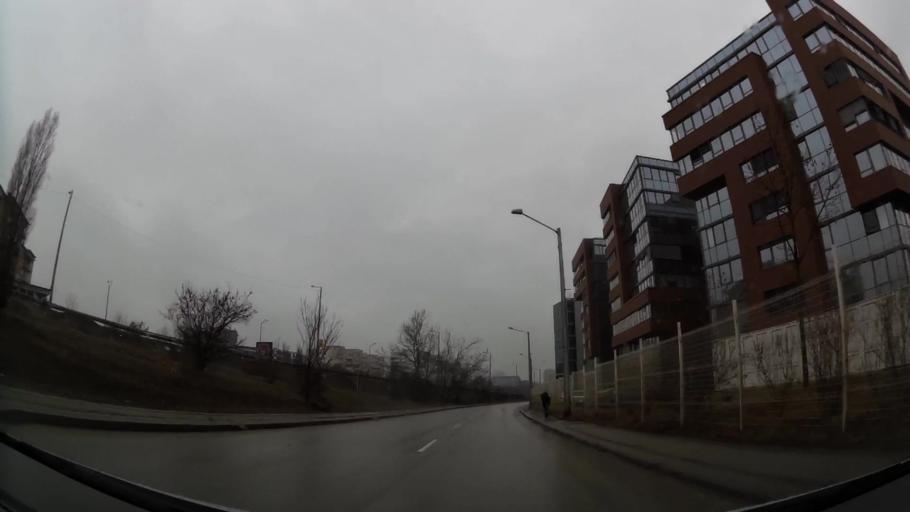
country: BG
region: Sofia-Capital
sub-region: Stolichna Obshtina
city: Sofia
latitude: 42.6259
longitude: 23.3737
